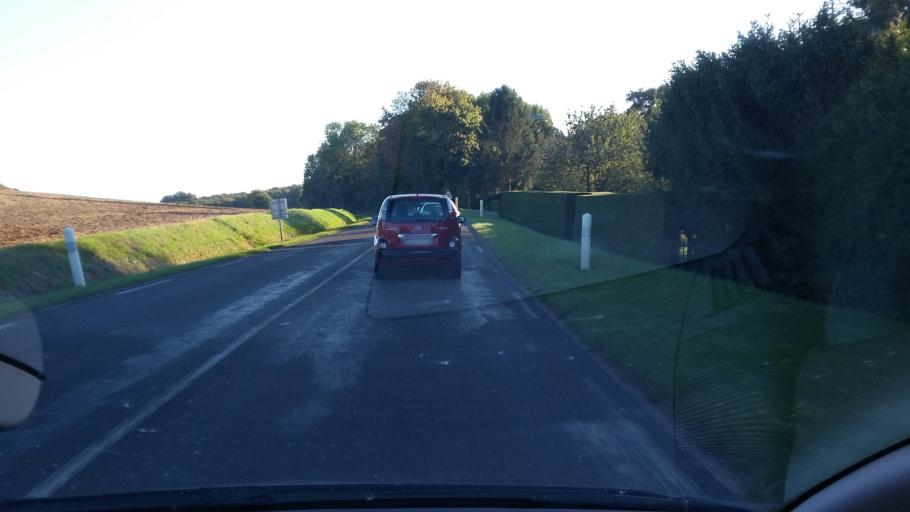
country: FR
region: Champagne-Ardenne
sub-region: Departement de la Marne
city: Verzenay
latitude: 49.1195
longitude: 4.1091
